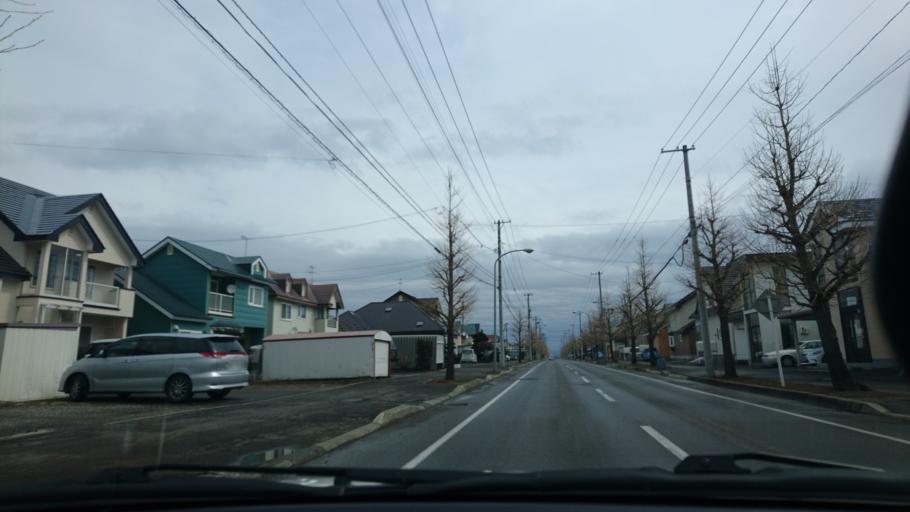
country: JP
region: Hokkaido
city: Otofuke
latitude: 42.9614
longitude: 143.1938
